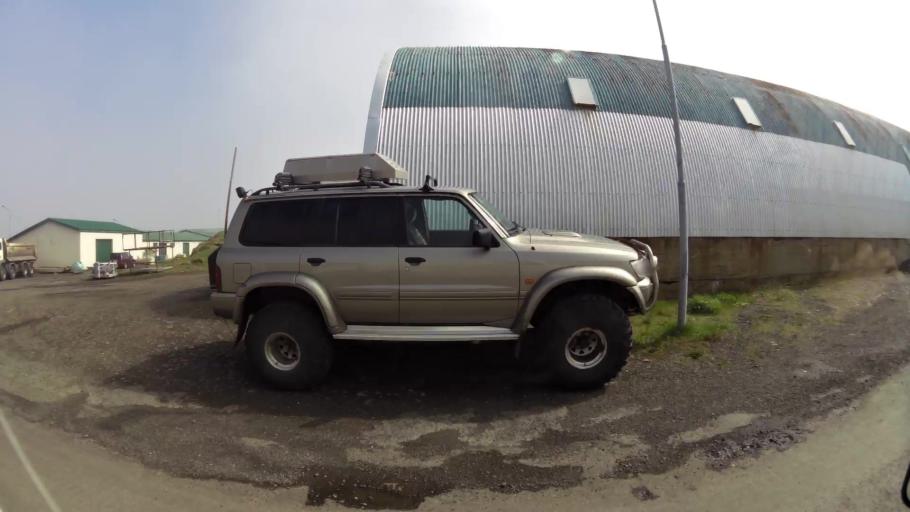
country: IS
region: East
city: Reydarfjoerdur
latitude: 64.6586
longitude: -14.2846
